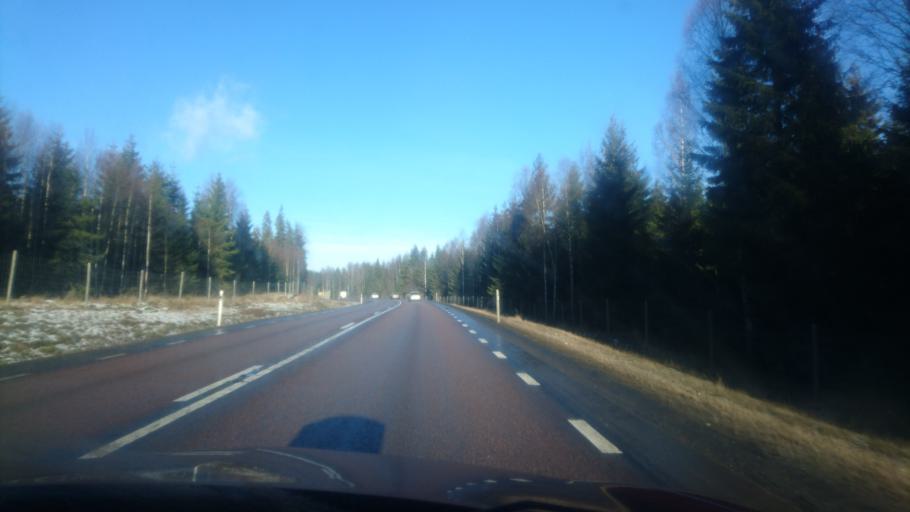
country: SE
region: Vaermland
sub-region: Sunne Kommun
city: Sunne
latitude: 59.7624
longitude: 13.1125
